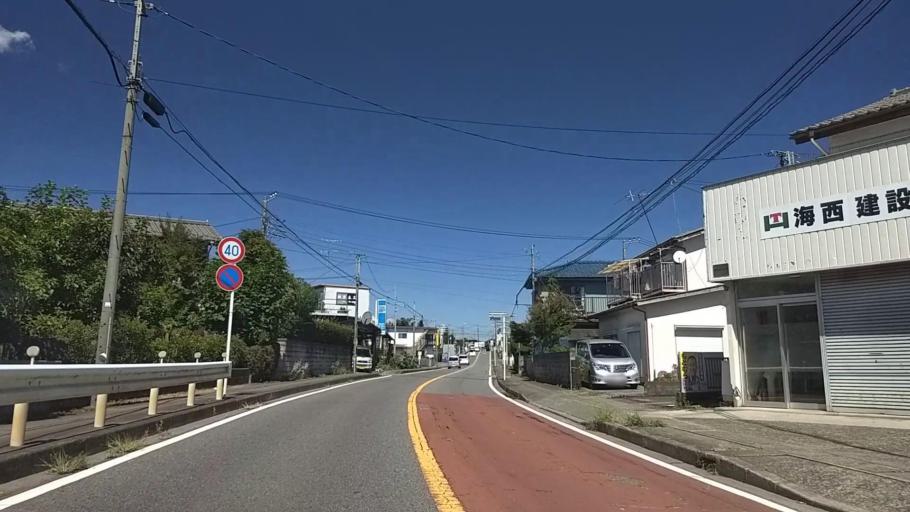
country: JP
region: Tokyo
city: Hachioji
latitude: 35.5764
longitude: 139.3155
